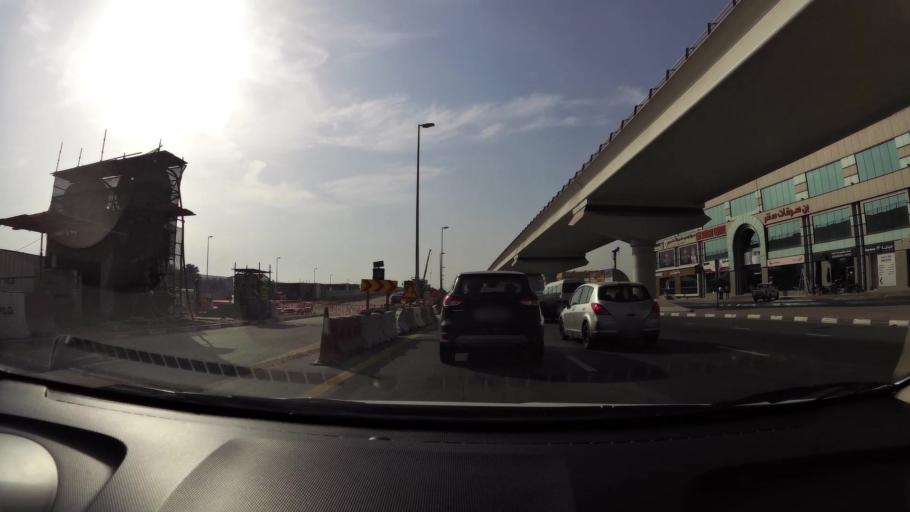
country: AE
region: Ash Shariqah
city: Sharjah
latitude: 25.2328
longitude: 55.3862
